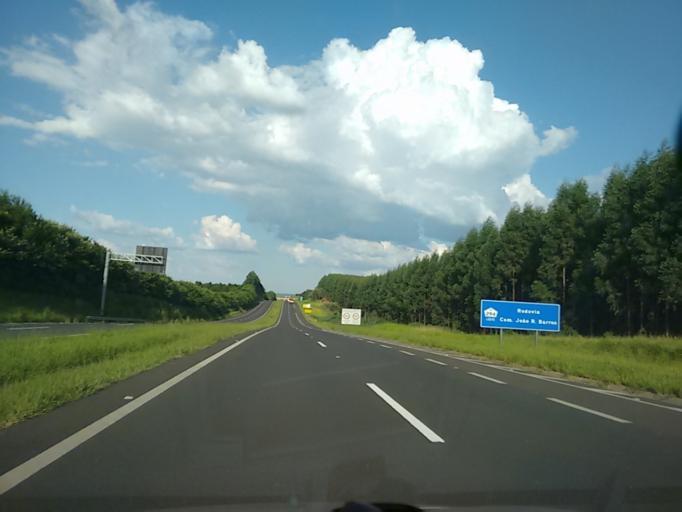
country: BR
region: Sao Paulo
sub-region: Duartina
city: Duartina
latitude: -22.3293
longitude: -49.4483
